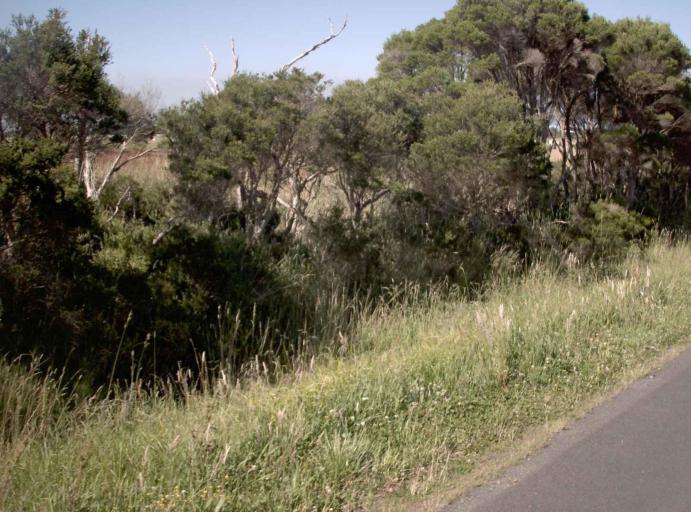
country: AU
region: Victoria
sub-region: Latrobe
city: Traralgon
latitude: -38.6275
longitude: 146.6211
